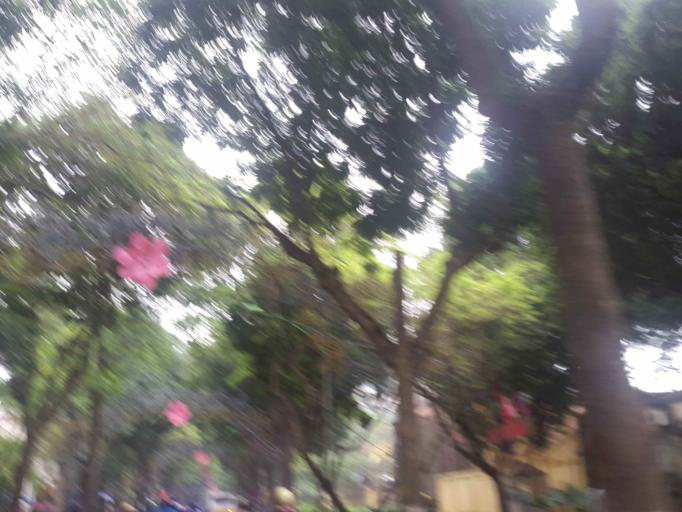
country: VN
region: Ha Noi
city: Hoan Kiem
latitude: 21.0409
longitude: 105.8404
